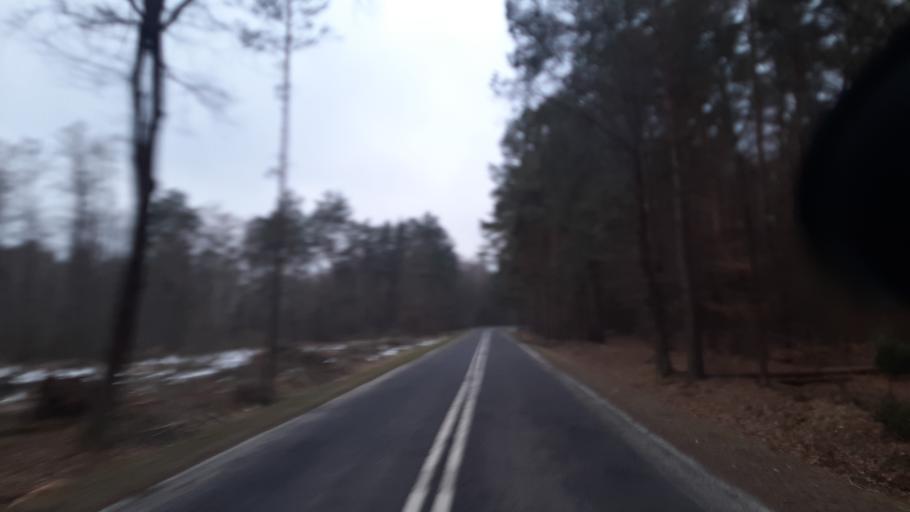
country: PL
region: Lublin Voivodeship
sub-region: Powiat parczewski
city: Podedworze
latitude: 51.5653
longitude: 23.2656
